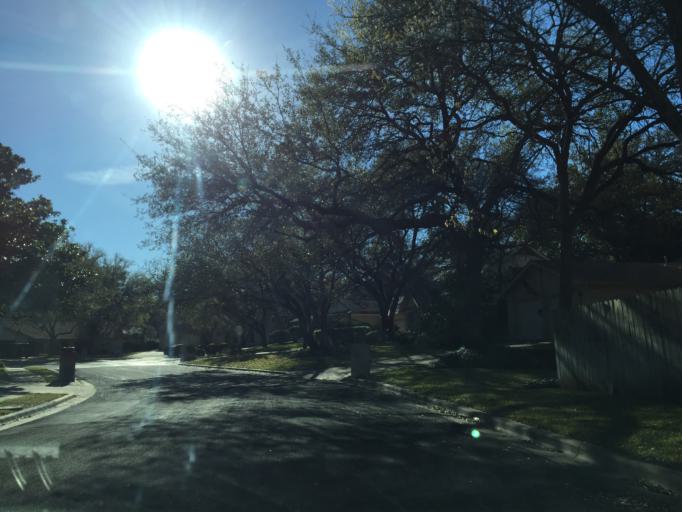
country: US
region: Texas
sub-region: Williamson County
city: Jollyville
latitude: 30.4079
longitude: -97.7378
